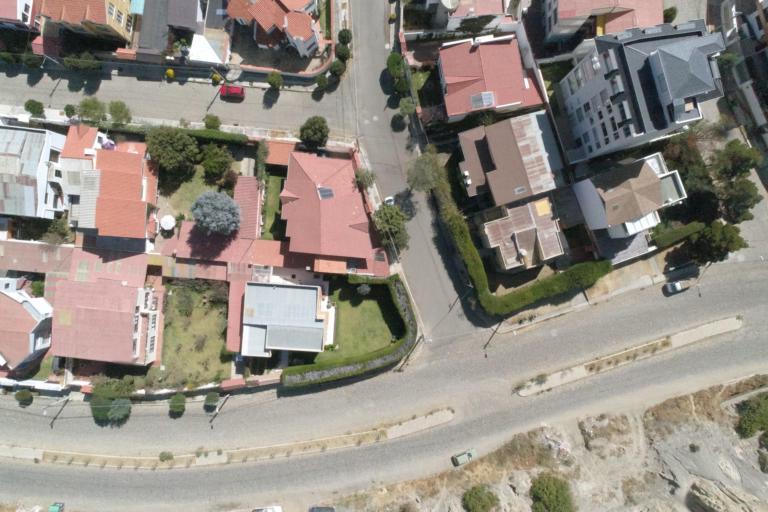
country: BO
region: La Paz
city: La Paz
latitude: -16.5325
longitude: -68.0702
